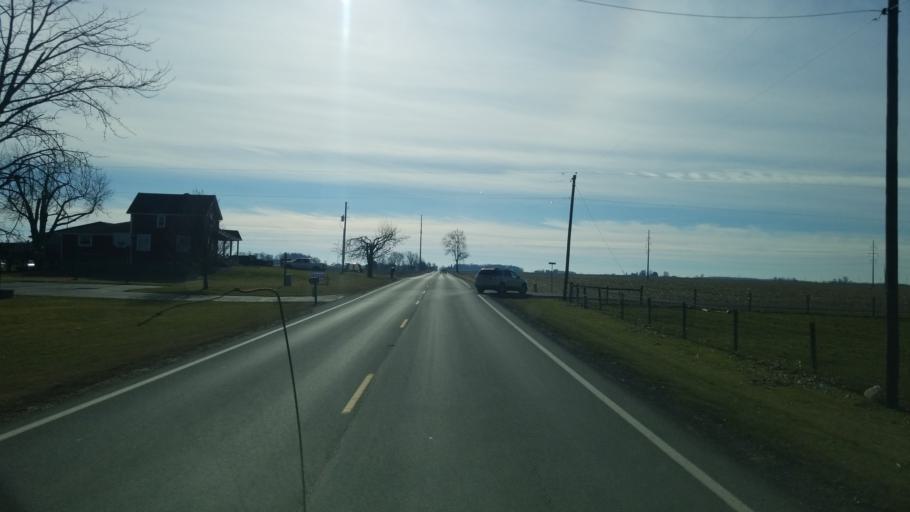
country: US
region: Ohio
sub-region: Putnam County
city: Leipsic
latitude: 41.0879
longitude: -83.9865
